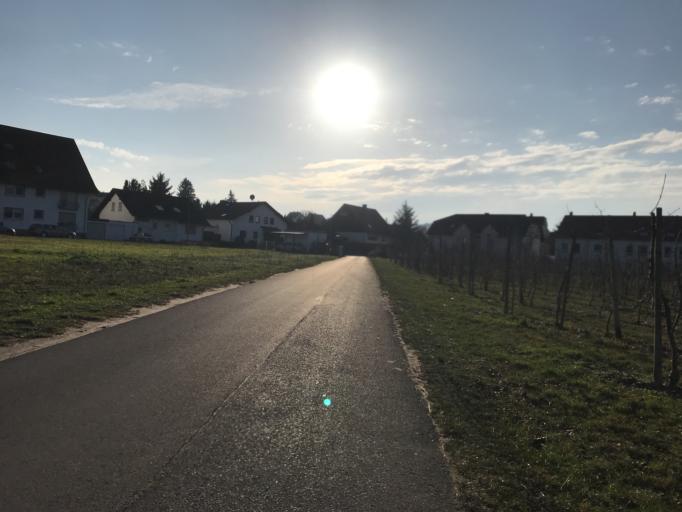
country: DE
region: Rheinland-Pfalz
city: Wackernheim
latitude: 50.0012
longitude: 8.1206
